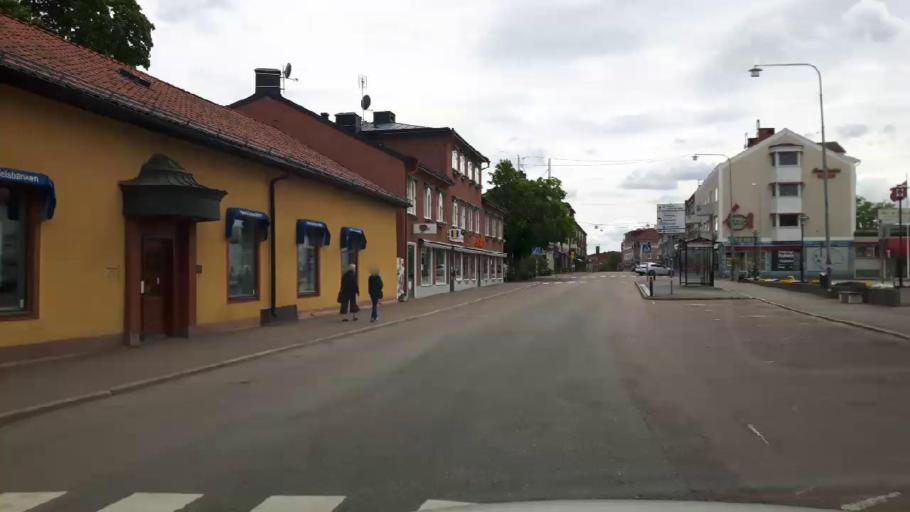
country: SE
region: Dalarna
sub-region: Hedemora Kommun
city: Hedemora
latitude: 60.2779
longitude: 15.9854
